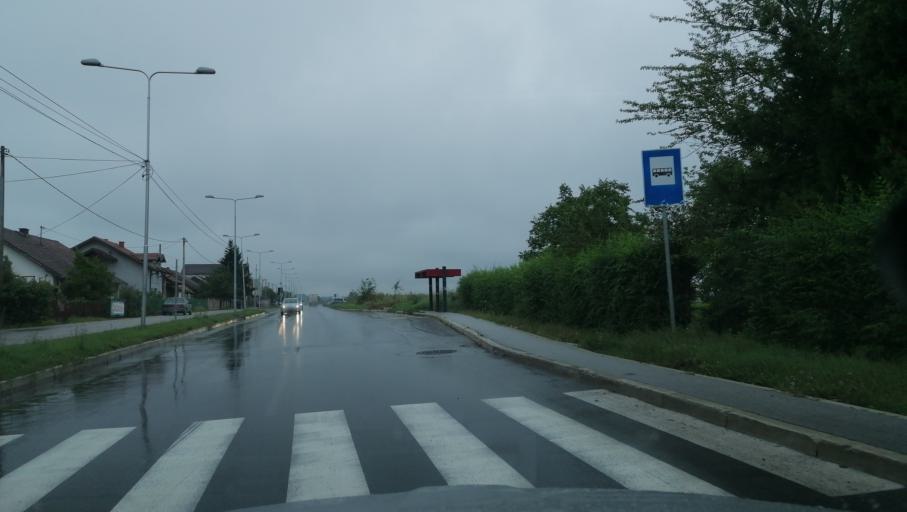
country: RS
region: Central Serbia
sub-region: Raski Okrug
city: Kraljevo
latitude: 43.7293
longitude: 20.6721
